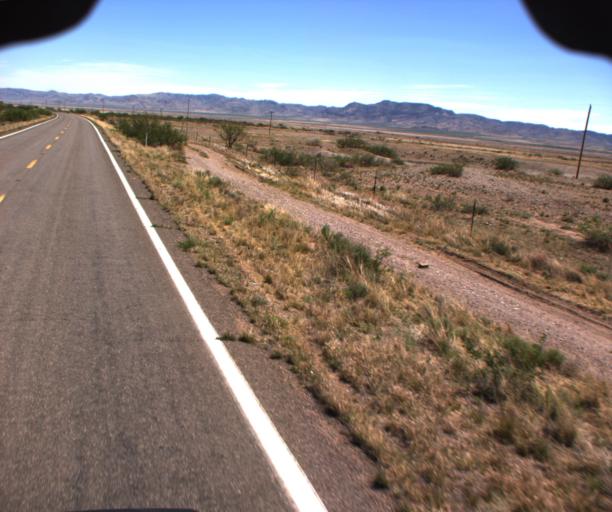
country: US
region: Arizona
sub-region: Cochise County
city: Douglas
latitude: 31.6481
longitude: -109.1654
